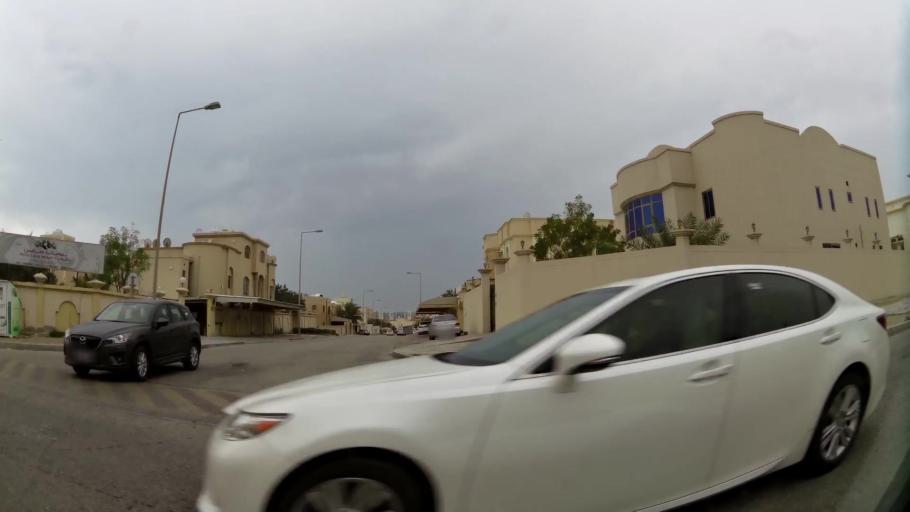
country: BH
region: Central Governorate
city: Madinat Hamad
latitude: 26.1144
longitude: 50.4995
